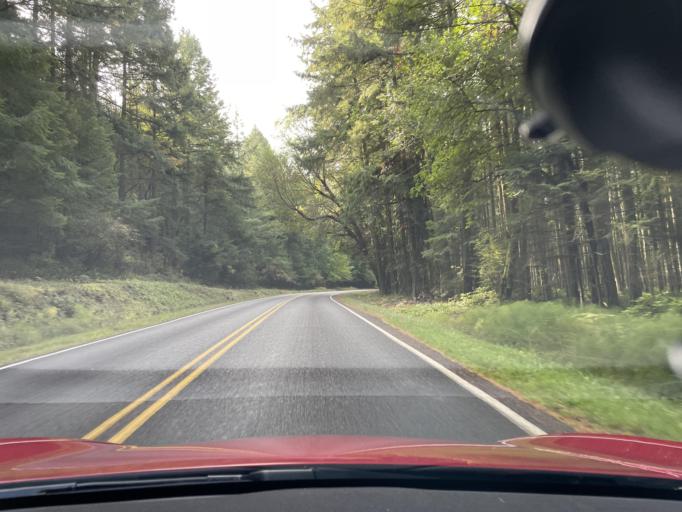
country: US
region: Washington
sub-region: San Juan County
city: Friday Harbor
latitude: 48.5895
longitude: -123.1391
